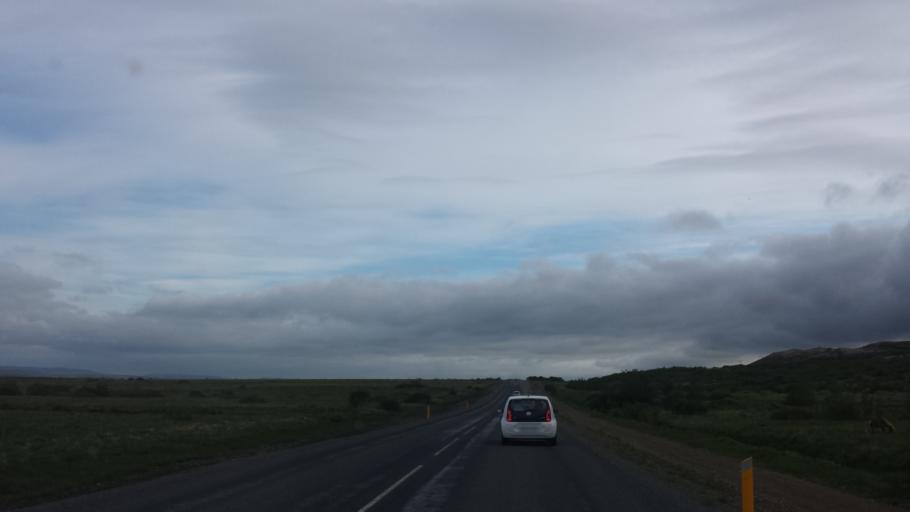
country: IS
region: South
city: Selfoss
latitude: 64.2930
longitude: -20.3359
